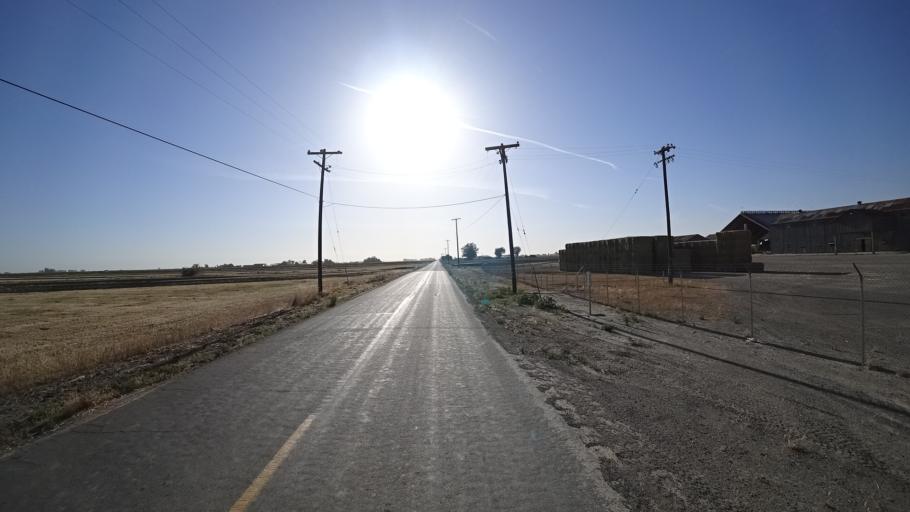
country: US
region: California
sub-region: Kings County
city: Stratford
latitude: 36.1673
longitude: -119.8122
